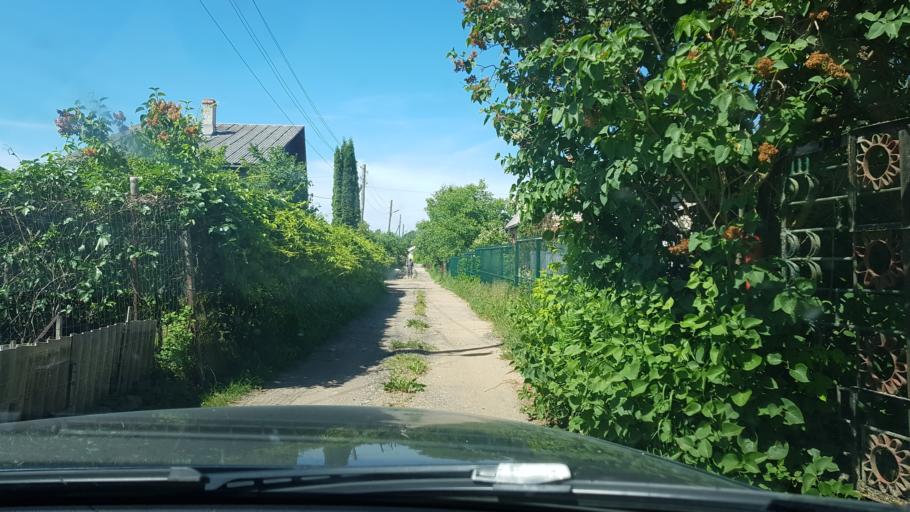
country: LV
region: Daugavpils
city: Daugavpils
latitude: 55.8604
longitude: 26.5733
